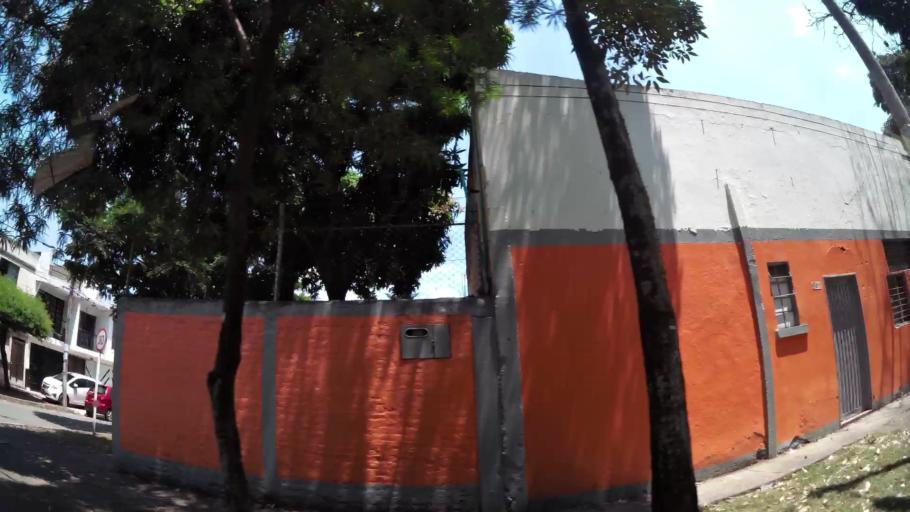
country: CO
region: Valle del Cauca
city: Cali
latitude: 3.4459
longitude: -76.4985
